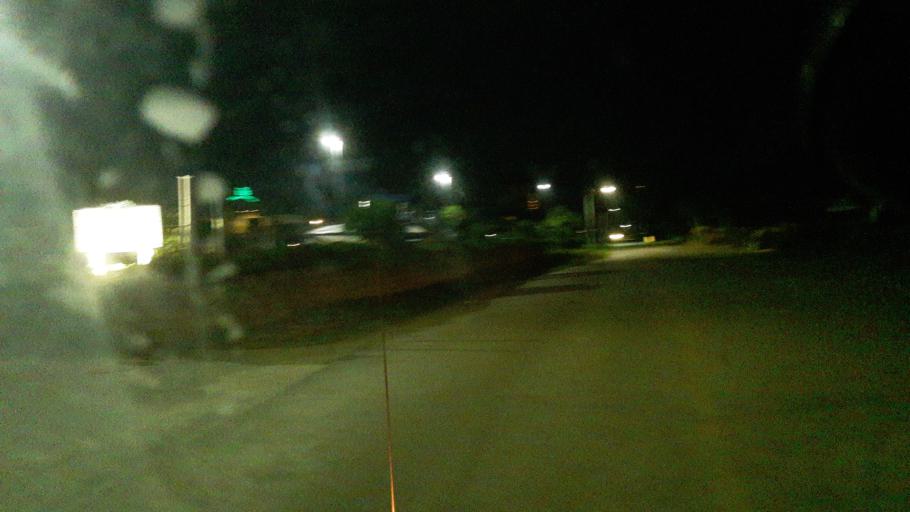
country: US
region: North Carolina
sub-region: Brunswick County
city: Sunset Beach
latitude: 33.8806
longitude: -78.4650
